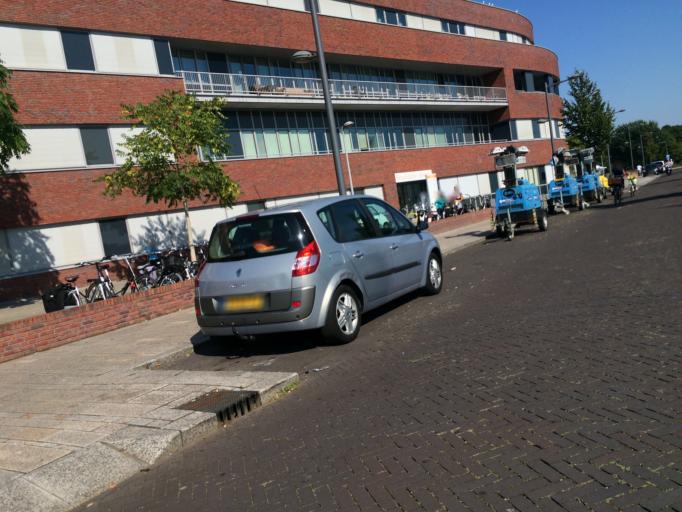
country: NL
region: Flevoland
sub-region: Gemeente Almere
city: Almere Stad
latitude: 52.3682
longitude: 5.2232
